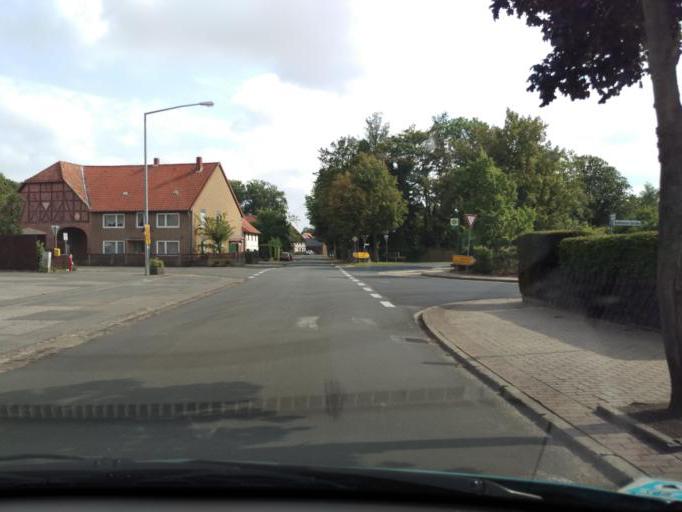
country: DE
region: Lower Saxony
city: Schellerten
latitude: 52.2263
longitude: 10.1249
